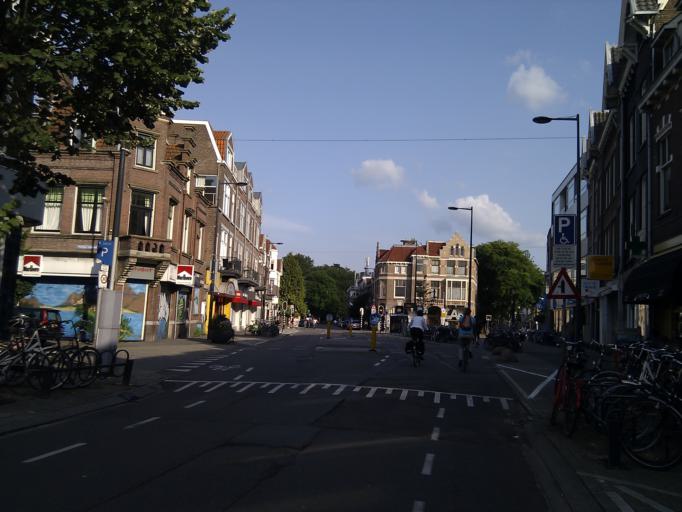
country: NL
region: Utrecht
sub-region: Gemeente Utrecht
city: Utrecht
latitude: 52.0898
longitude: 5.1352
